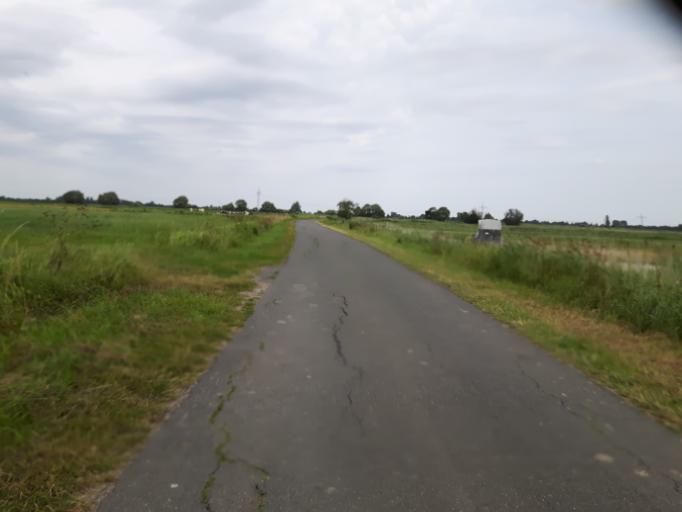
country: DE
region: Lower Saxony
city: Varel
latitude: 53.3688
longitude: 8.2086
